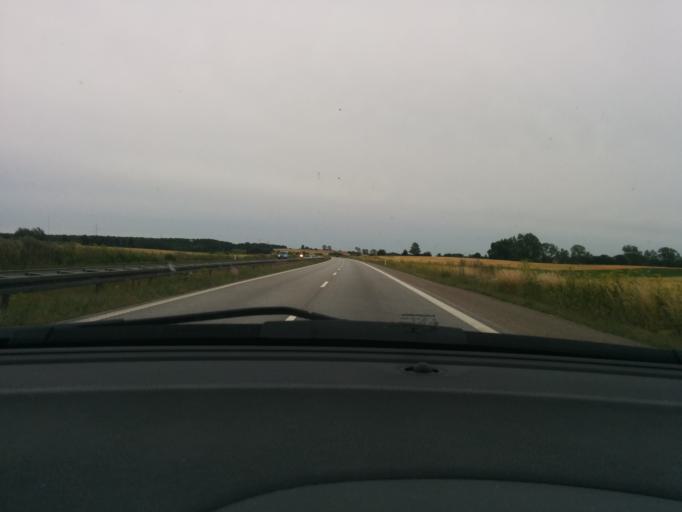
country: DK
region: Zealand
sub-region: Vordingborg Kommune
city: Orslev
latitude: 55.1089
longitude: 11.9358
